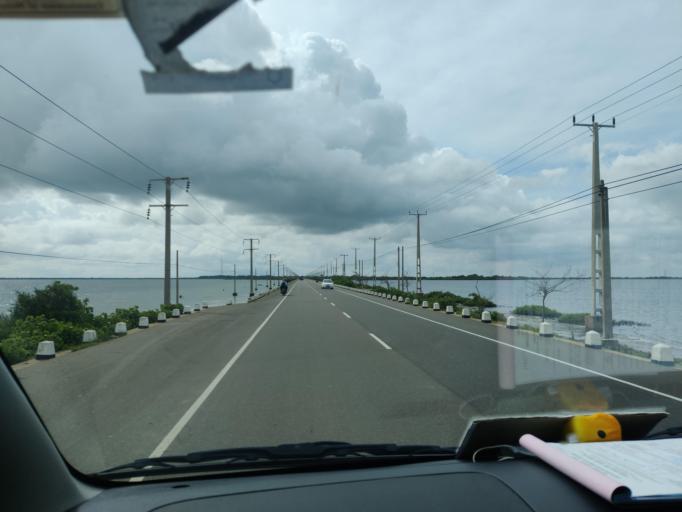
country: LK
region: Northern Province
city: Vavuniya
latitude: 8.9674
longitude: 79.9178
